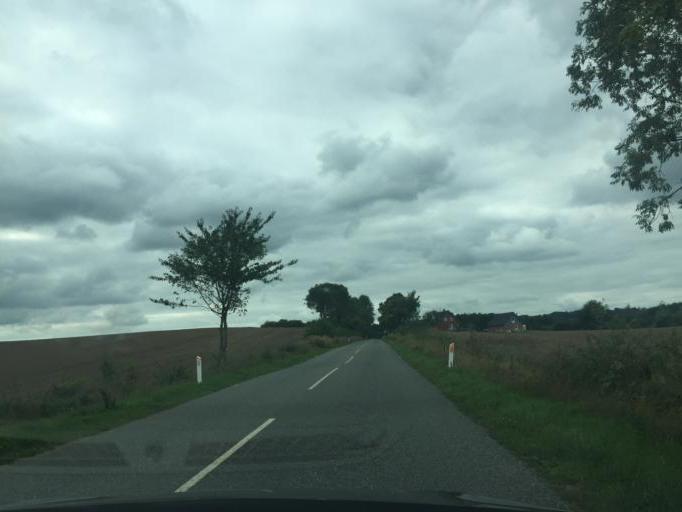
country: DK
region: South Denmark
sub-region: Assens Kommune
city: Tommerup
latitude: 55.3557
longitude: 10.2195
